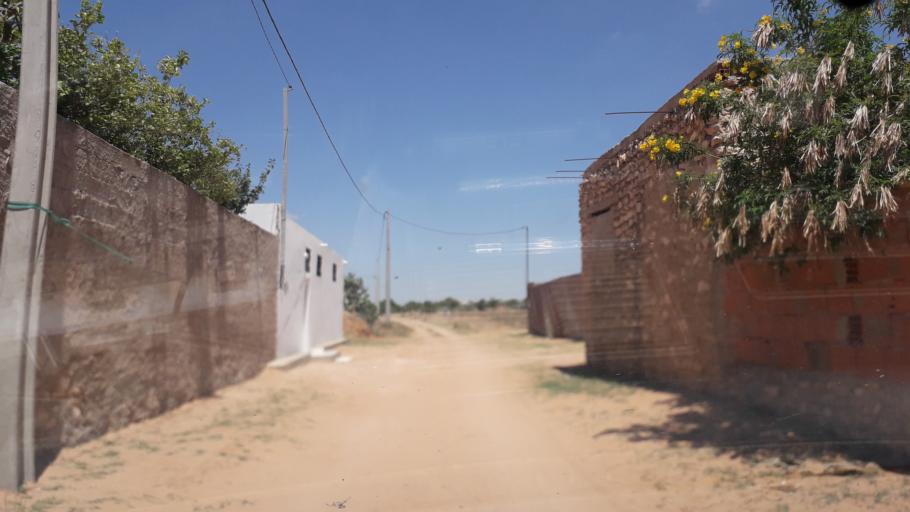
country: TN
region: Safaqis
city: Al Qarmadah
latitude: 34.8313
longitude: 10.7768
